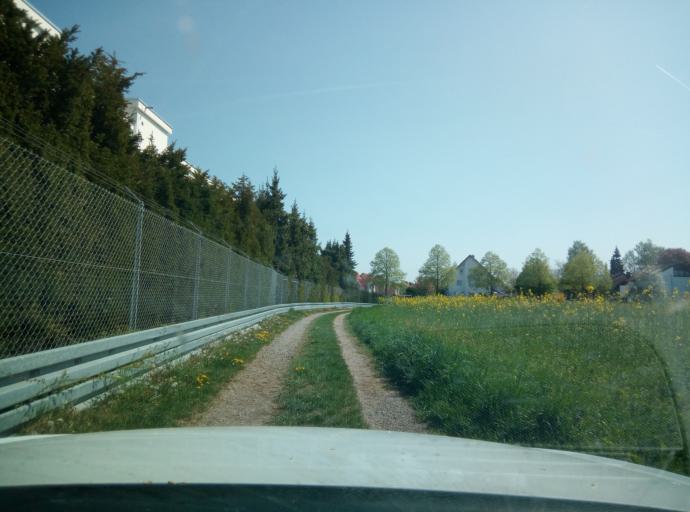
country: DE
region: Baden-Wuerttemberg
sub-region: Tuebingen Region
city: Kusterdingen
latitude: 48.5506
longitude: 9.1041
